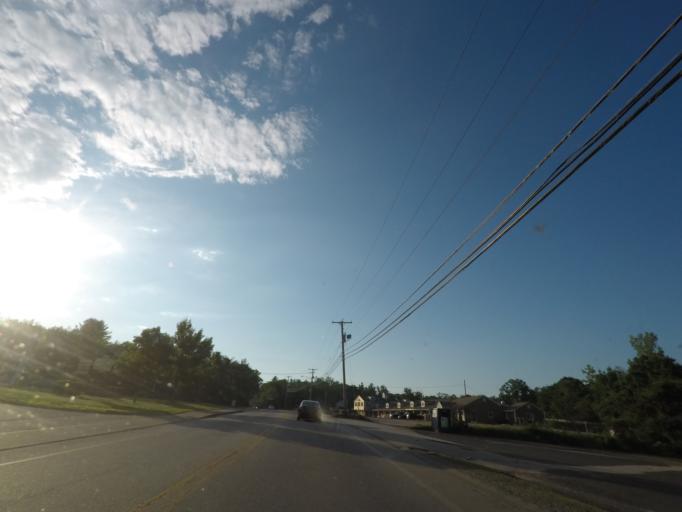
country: US
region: Massachusetts
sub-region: Worcester County
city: Sturbridge
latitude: 42.0928
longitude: -72.0680
